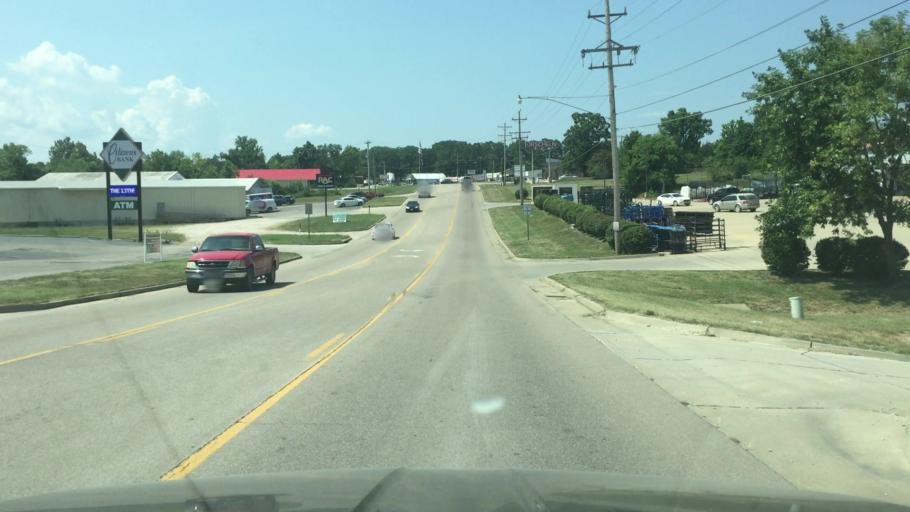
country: US
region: Missouri
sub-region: Miller County
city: Eldon
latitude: 38.3354
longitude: -92.5856
